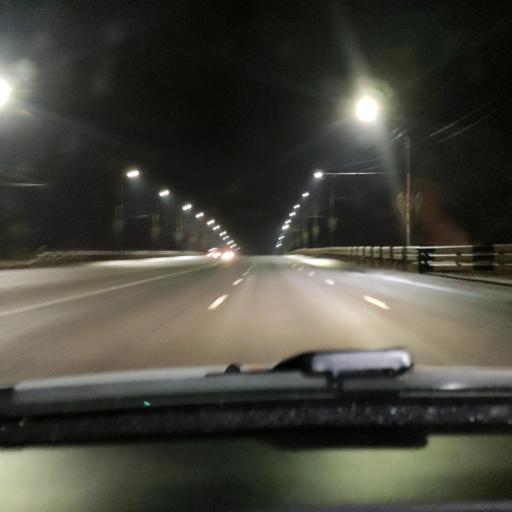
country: RU
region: Voronezj
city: Voronezh
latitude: 51.6345
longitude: 39.2196
